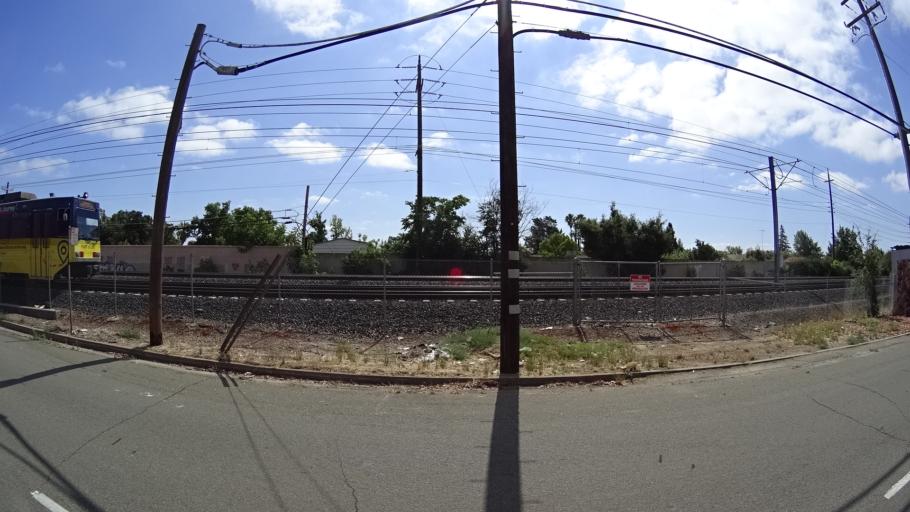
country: US
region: California
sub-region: Sacramento County
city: Parkway
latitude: 38.5352
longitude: -121.4833
